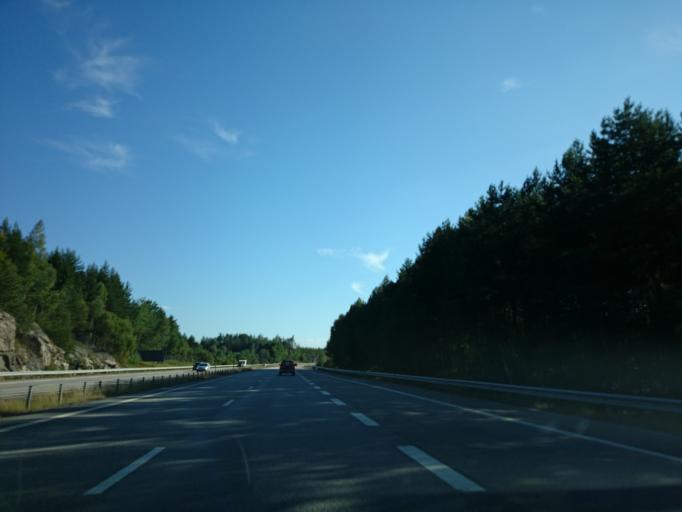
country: SE
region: Soedermanland
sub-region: Oxelosunds Kommun
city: Oxelosund
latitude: 58.8558
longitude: 17.2078
